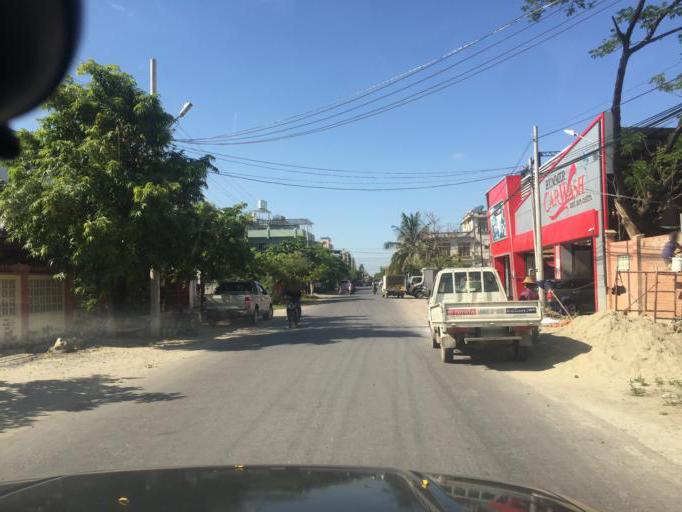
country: MM
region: Mandalay
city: Mandalay
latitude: 21.9580
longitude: 96.1100
